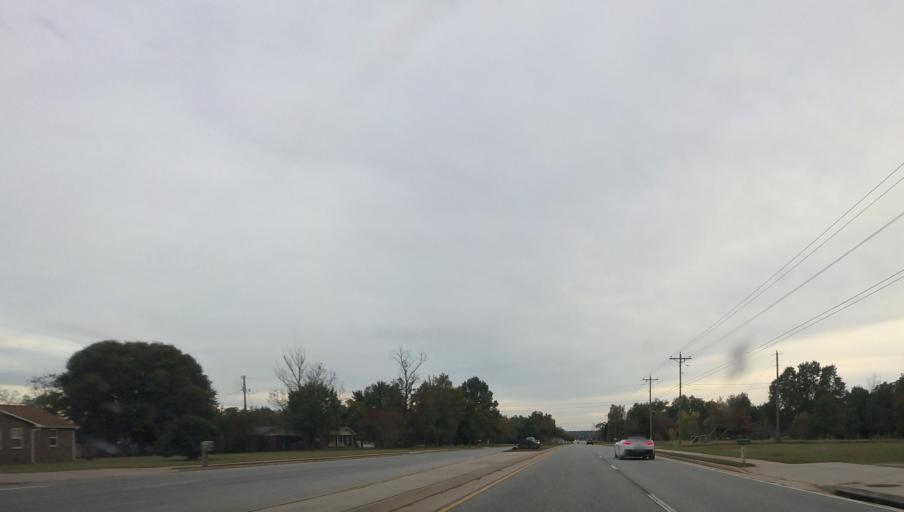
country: US
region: Georgia
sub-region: Houston County
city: Perry
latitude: 32.5124
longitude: -83.6625
